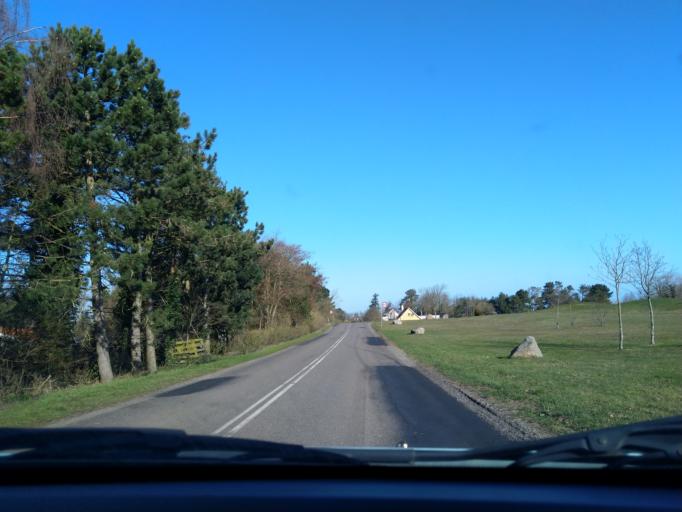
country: DK
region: Zealand
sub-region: Kalundborg Kommune
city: Kalundborg
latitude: 55.7166
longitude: 11.0141
